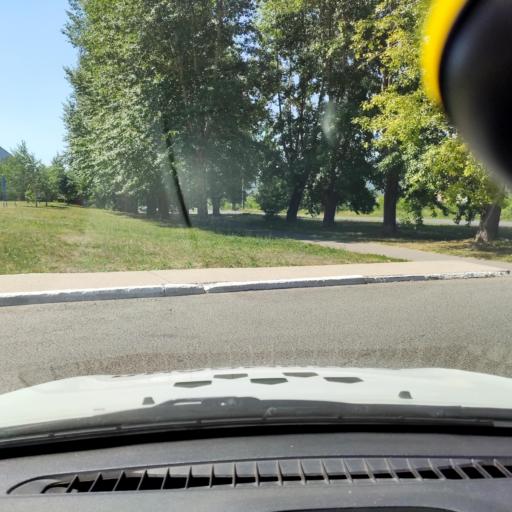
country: RU
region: Samara
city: Zhigulevsk
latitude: 53.4147
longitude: 49.5300
